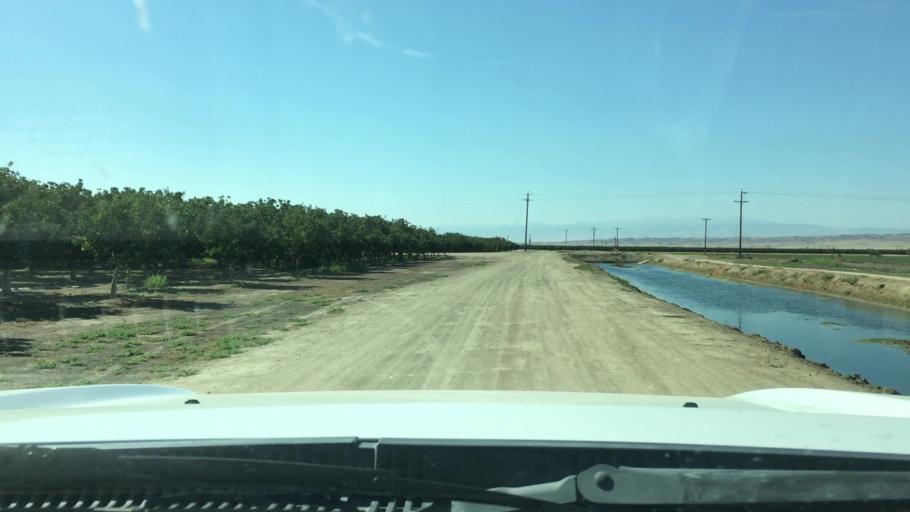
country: US
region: California
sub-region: Kern County
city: Buttonwillow
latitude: 35.3707
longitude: -119.3996
